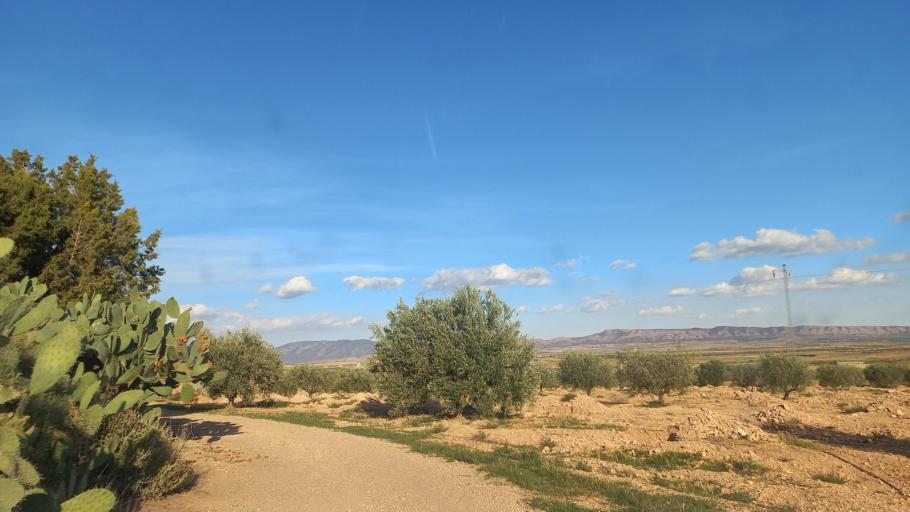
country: TN
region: Al Qasrayn
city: Sbiba
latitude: 35.3810
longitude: 9.0187
